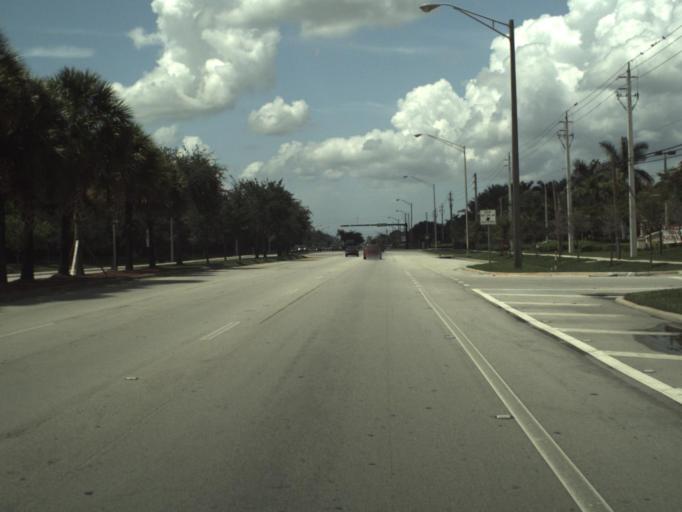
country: US
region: Florida
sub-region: Broward County
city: Parkland
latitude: 26.3062
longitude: -80.2021
